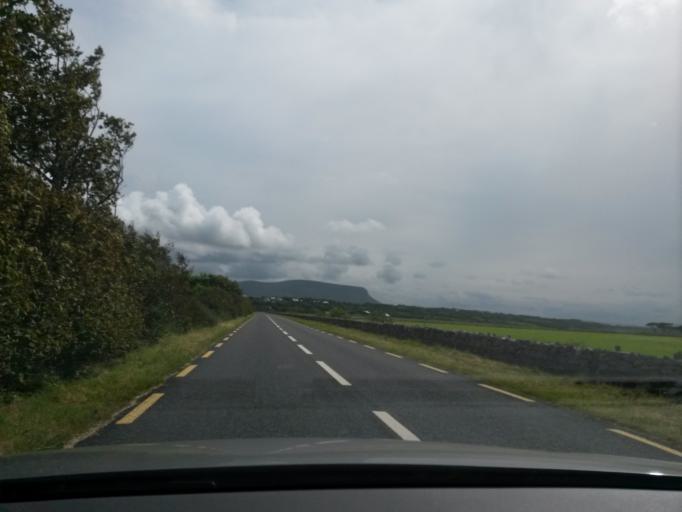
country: IE
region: Connaught
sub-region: County Leitrim
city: Kinlough
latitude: 54.4416
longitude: -8.4550
